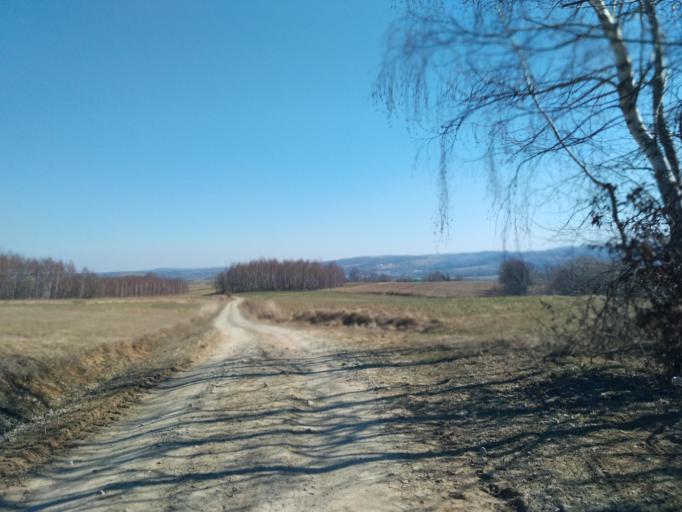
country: PL
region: Subcarpathian Voivodeship
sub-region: Powiat ropczycko-sedziszowski
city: Niedzwiada
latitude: 49.9540
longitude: 21.5566
